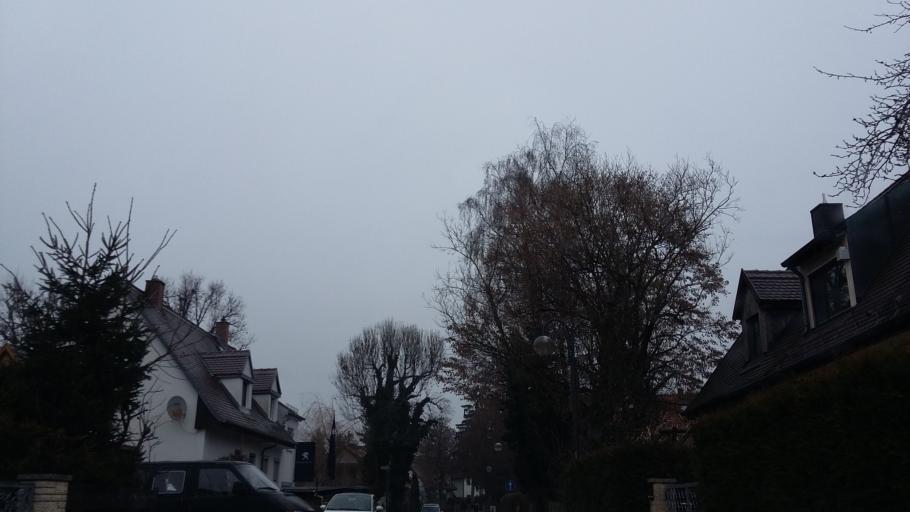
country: DE
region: Bavaria
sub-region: Upper Bavaria
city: Eichenau
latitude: 48.1743
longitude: 11.3284
